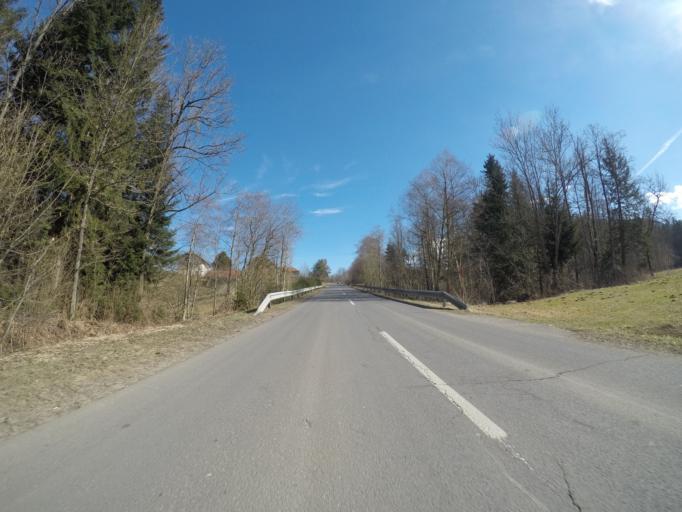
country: SI
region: Lovrenc na Pohorju
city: Lovrenc na Pohorju
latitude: 46.5415
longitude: 15.4247
